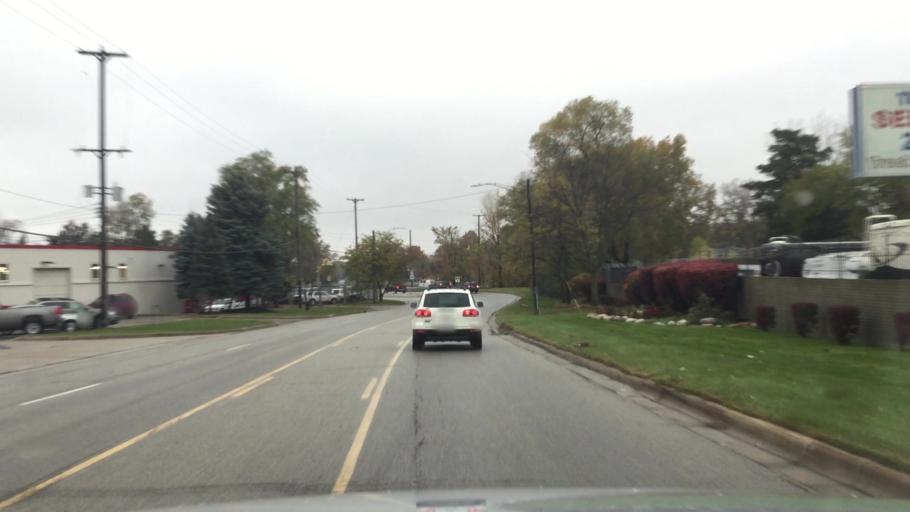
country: US
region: Michigan
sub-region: Oakland County
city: Sylvan Lake
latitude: 42.6212
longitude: -83.3226
